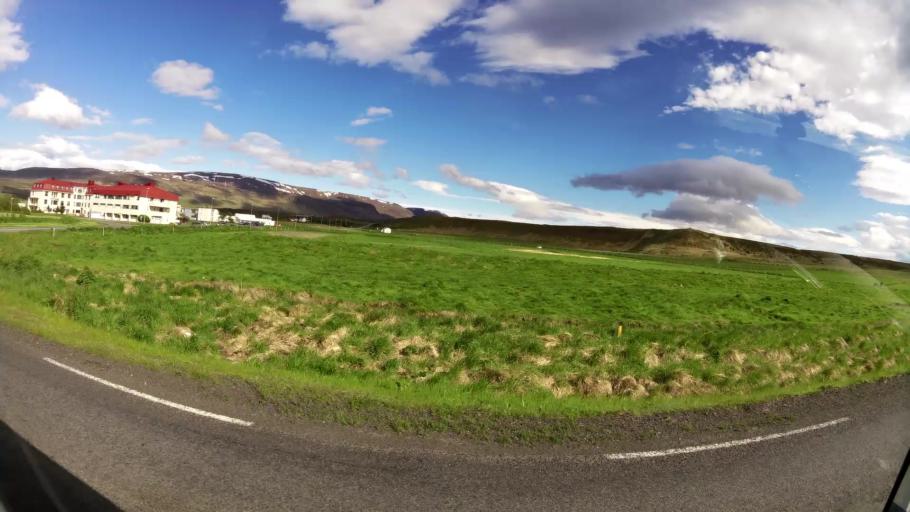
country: IS
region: Northwest
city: Saudarkrokur
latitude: 65.6560
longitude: -20.2847
